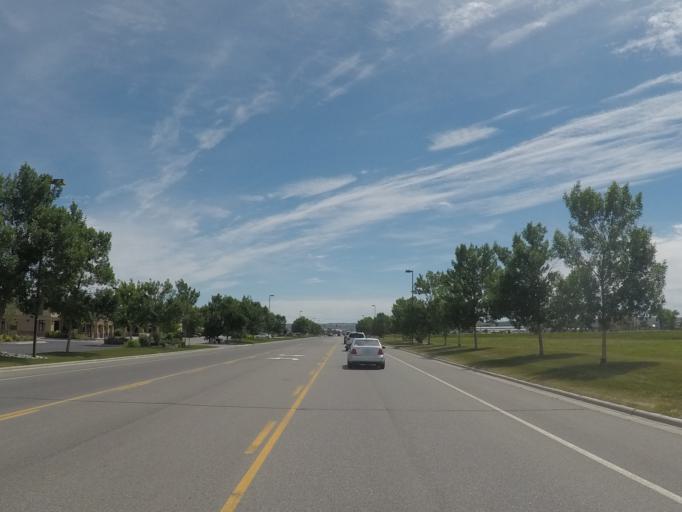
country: US
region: Montana
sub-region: Yellowstone County
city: Billings
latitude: 45.7442
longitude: -108.6017
